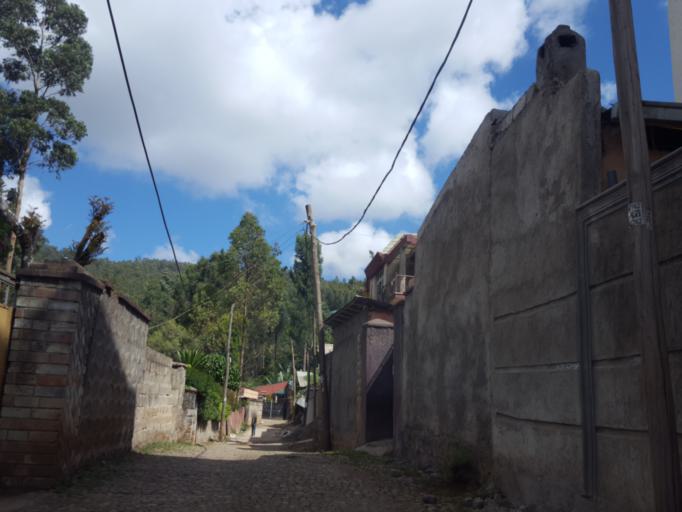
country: ET
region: Adis Abeba
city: Addis Ababa
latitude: 9.0728
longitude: 38.7375
